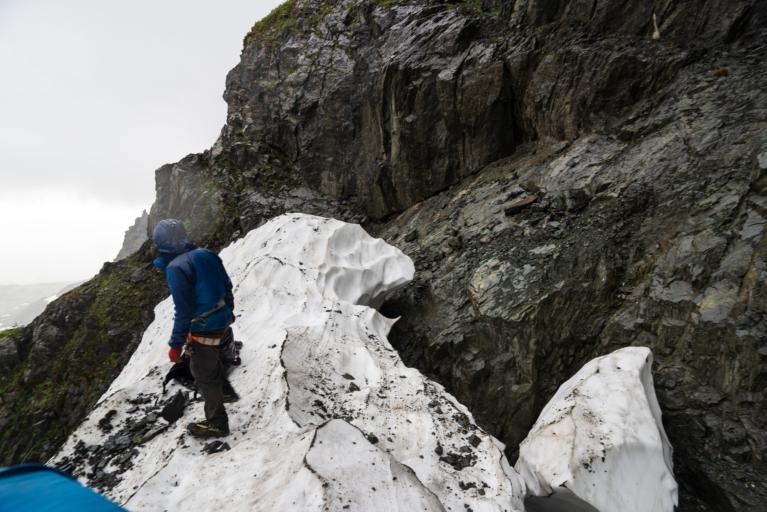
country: RU
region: Komi Republic
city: Synya
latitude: 64.7804
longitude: 58.8837
